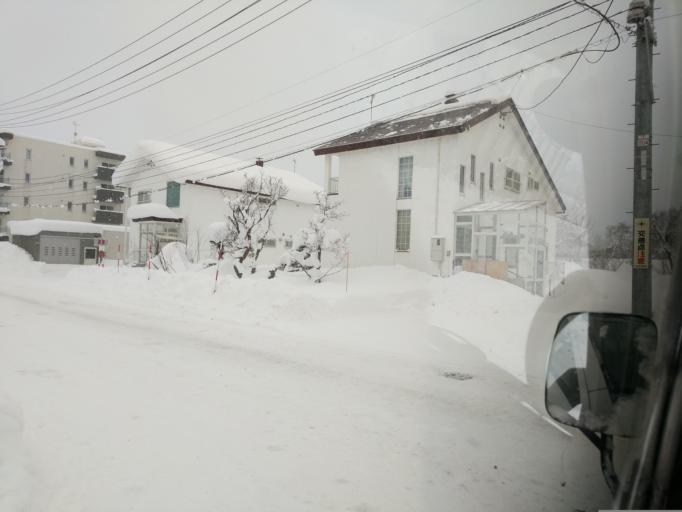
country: JP
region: Hokkaido
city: Niseko Town
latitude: 42.8967
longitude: 140.7460
